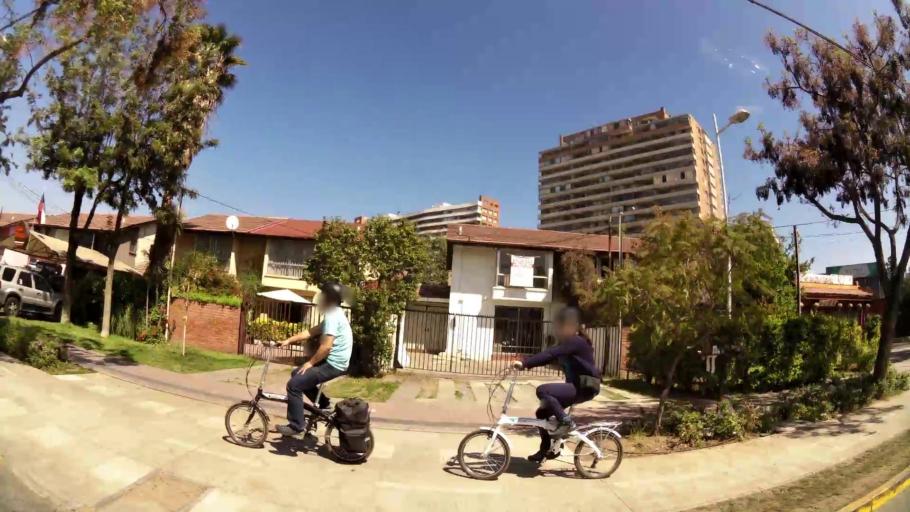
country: CL
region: Santiago Metropolitan
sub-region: Provincia de Santiago
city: Villa Presidente Frei, Nunoa, Santiago, Chile
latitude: -33.4191
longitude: -70.5524
